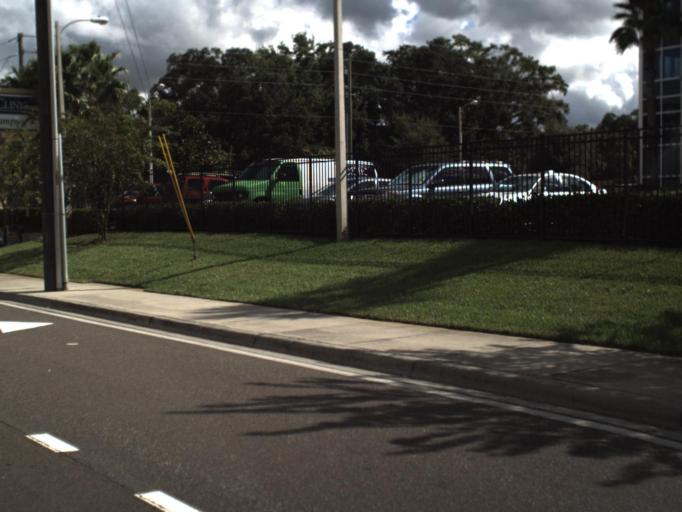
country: US
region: Florida
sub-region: Polk County
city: Lakeland
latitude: 28.0692
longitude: -81.9573
